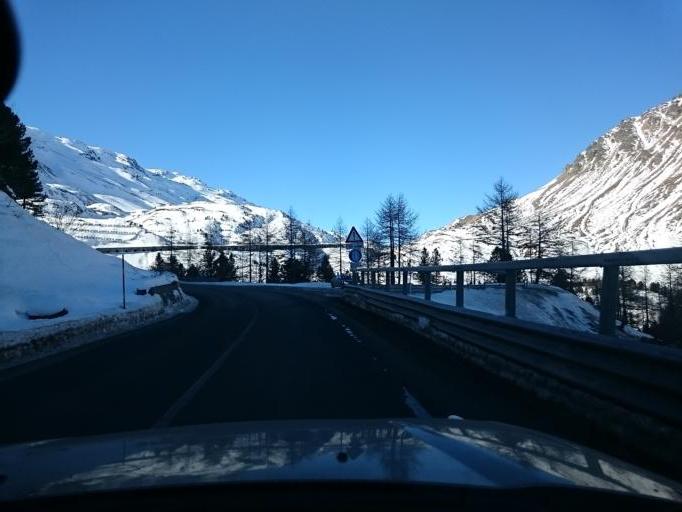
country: IT
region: Lombardy
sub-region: Provincia di Sondrio
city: Isolaccia
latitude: 46.4844
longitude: 10.2289
